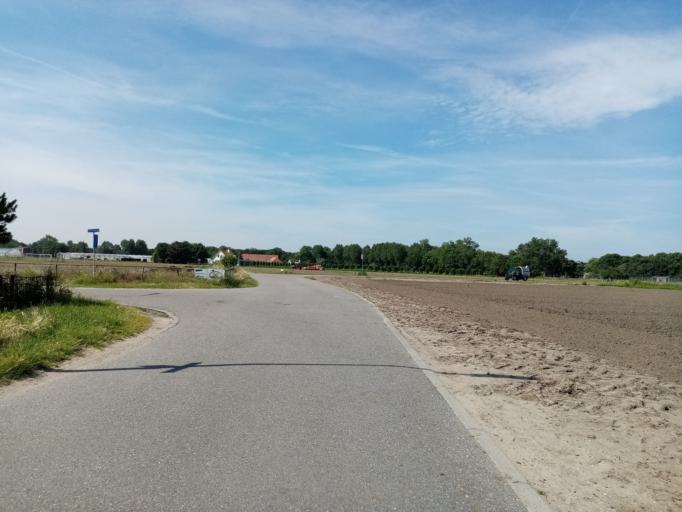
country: NL
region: South Holland
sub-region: Gemeente Noordwijk
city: Noordwijk-Binnen
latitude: 52.2289
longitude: 4.4307
